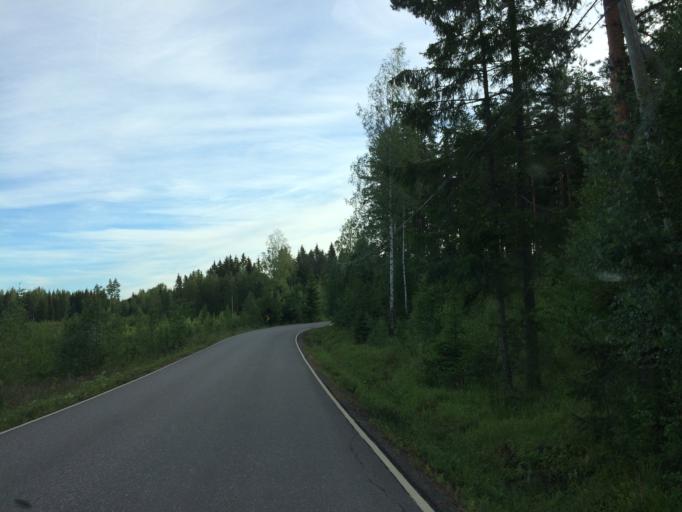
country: FI
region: Haeme
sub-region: Haemeenlinna
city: Janakkala
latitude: 60.8539
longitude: 24.5280
